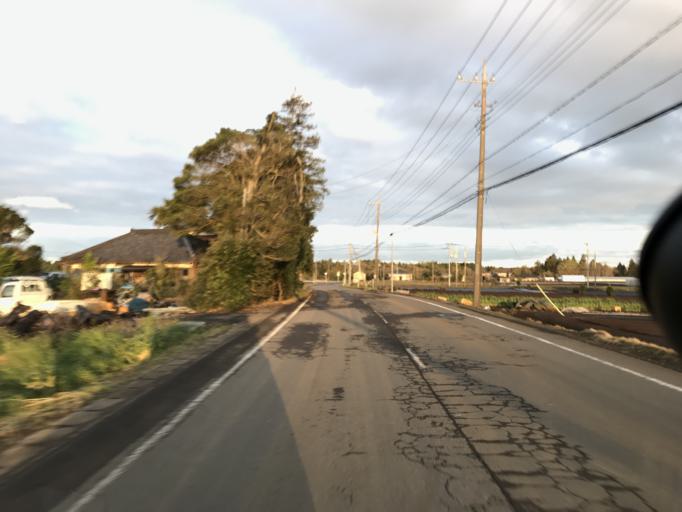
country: JP
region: Chiba
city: Sawara
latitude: 35.8264
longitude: 140.4743
